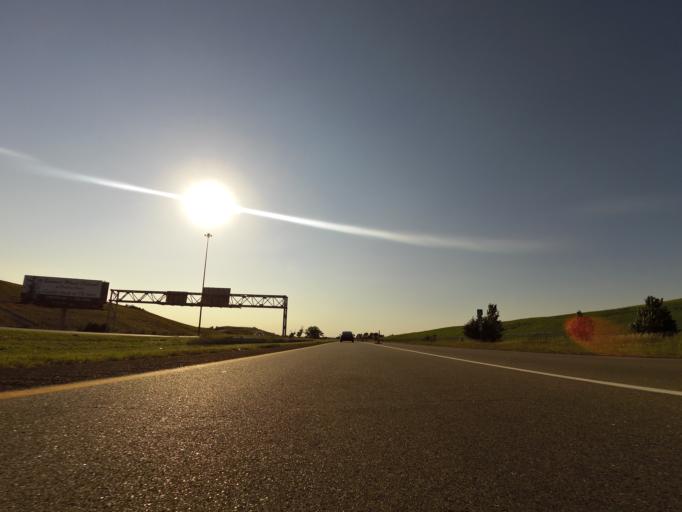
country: US
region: Kansas
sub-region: Sedgwick County
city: Maize
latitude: 37.7572
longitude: -97.3919
